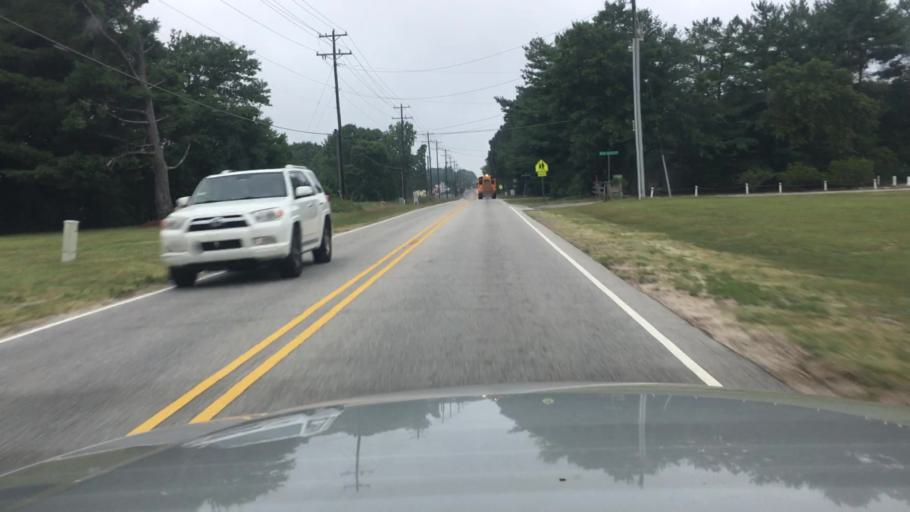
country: US
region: North Carolina
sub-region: Cumberland County
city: Hope Mills
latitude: 34.9764
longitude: -78.9793
